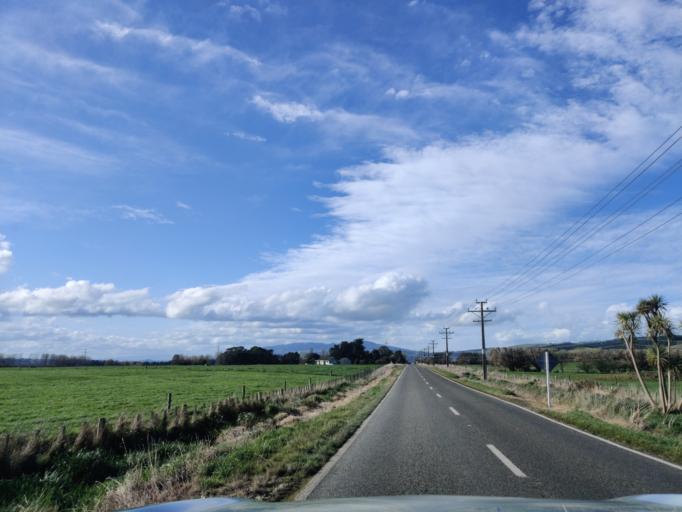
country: NZ
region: Manawatu-Wanganui
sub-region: Palmerston North City
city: Palmerston North
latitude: -40.3478
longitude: 175.7036
